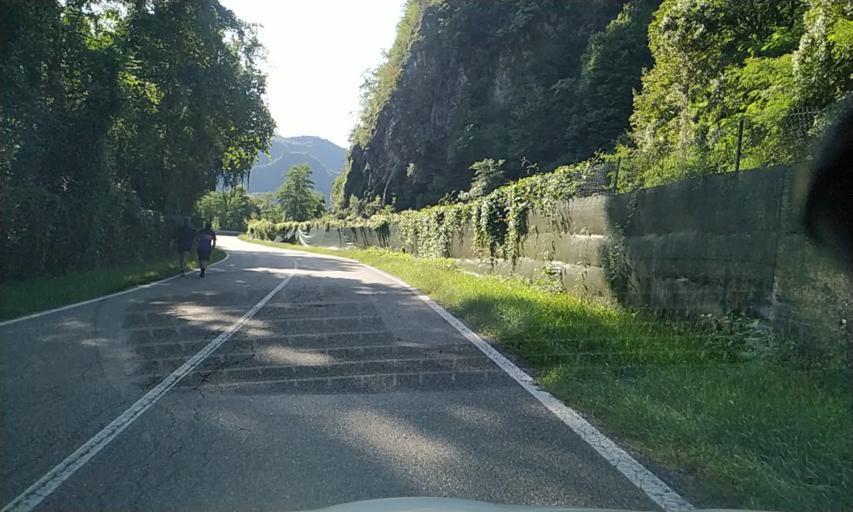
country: IT
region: Piedmont
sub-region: Provincia di Vercelli
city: Varallo
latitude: 45.8000
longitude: 8.2619
